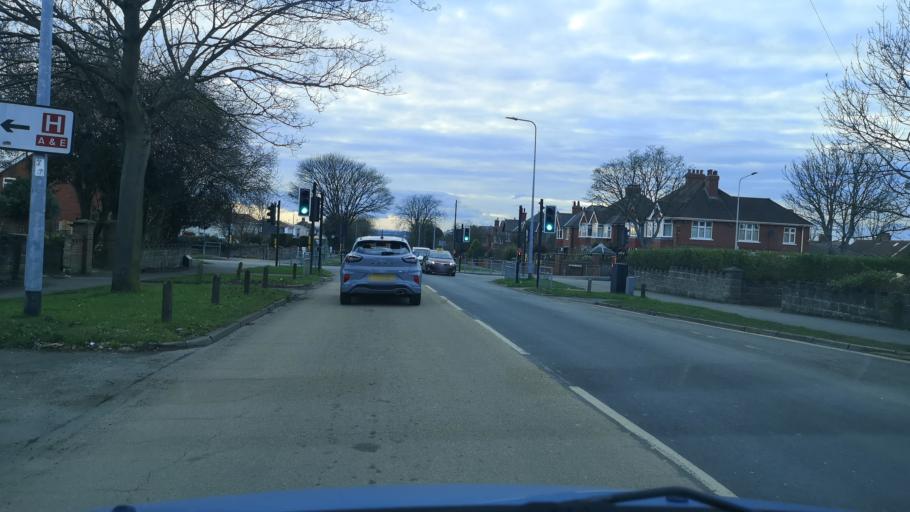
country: GB
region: England
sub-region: North Lincolnshire
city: Scunthorpe
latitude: 53.5902
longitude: -0.6677
